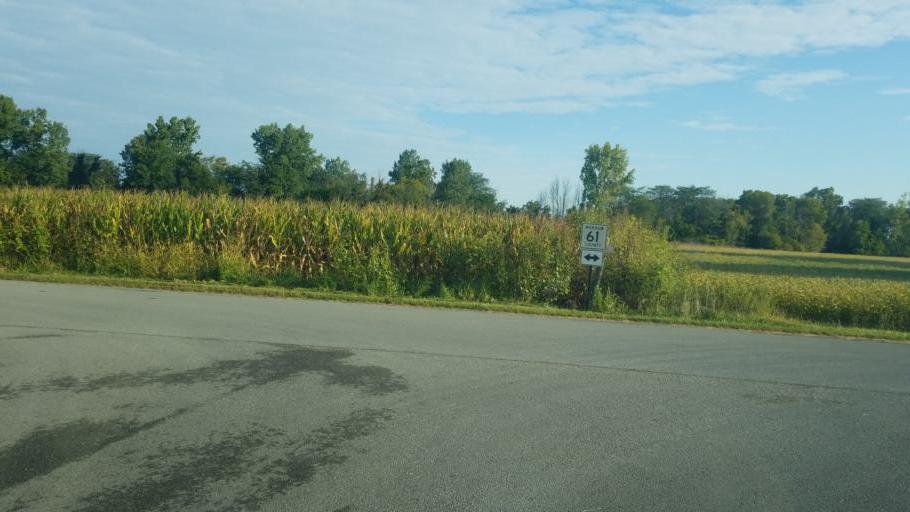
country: US
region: Ohio
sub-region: Morrow County
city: Cardington
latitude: 40.6162
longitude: -82.9379
